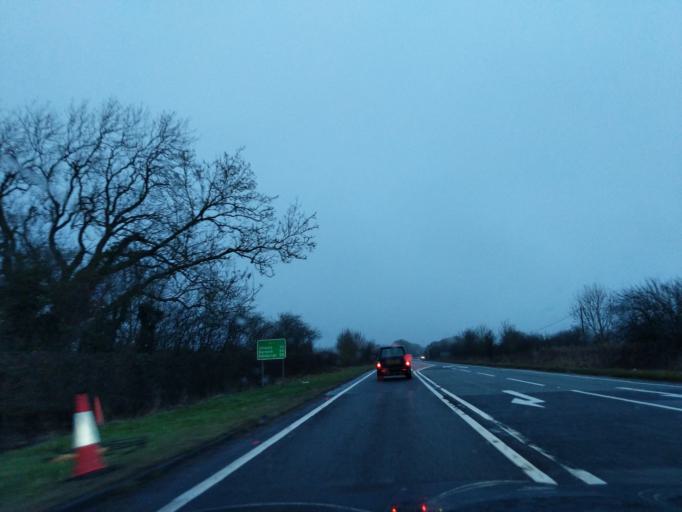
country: GB
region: England
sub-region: Northumberland
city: Felton
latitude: 55.2833
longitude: -1.7273
